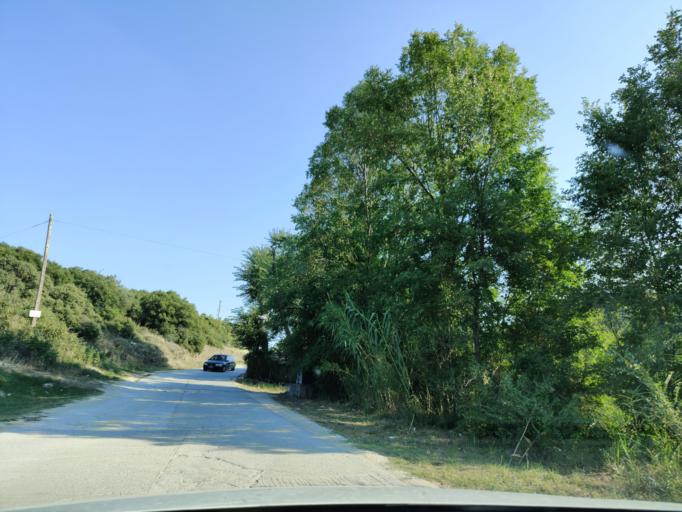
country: GR
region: East Macedonia and Thrace
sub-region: Nomos Kavalas
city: Nea Peramos
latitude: 40.8247
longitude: 24.3073
